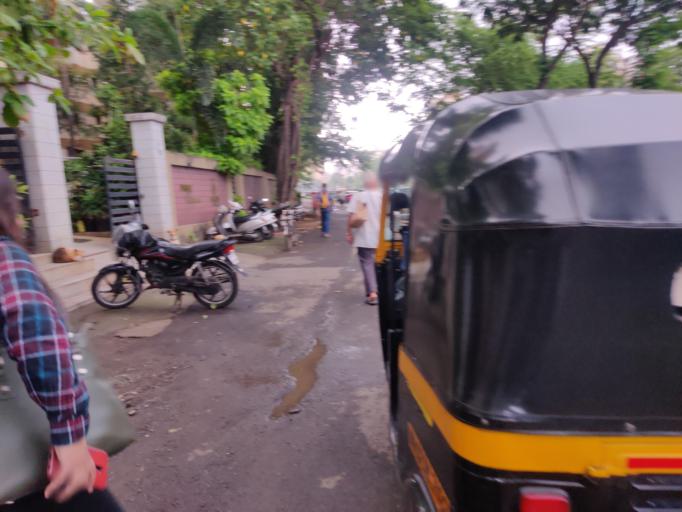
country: IN
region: Maharashtra
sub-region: Mumbai Suburban
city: Borivli
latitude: 19.2518
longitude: 72.8564
